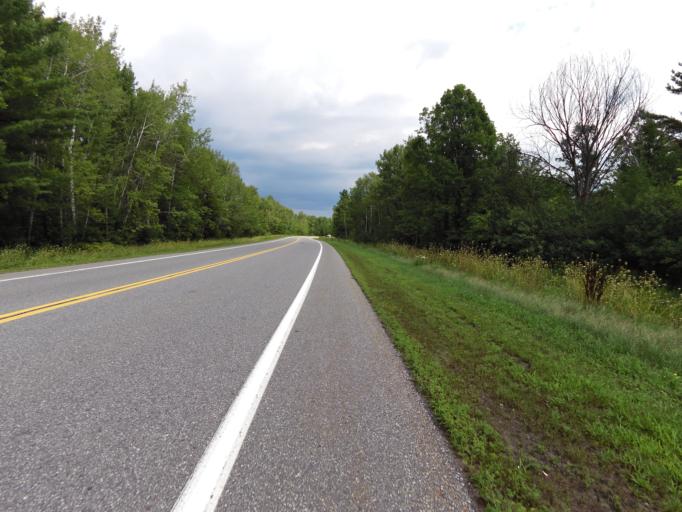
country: CA
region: Quebec
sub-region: Outaouais
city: Gatineau
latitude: 45.4687
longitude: -75.5795
